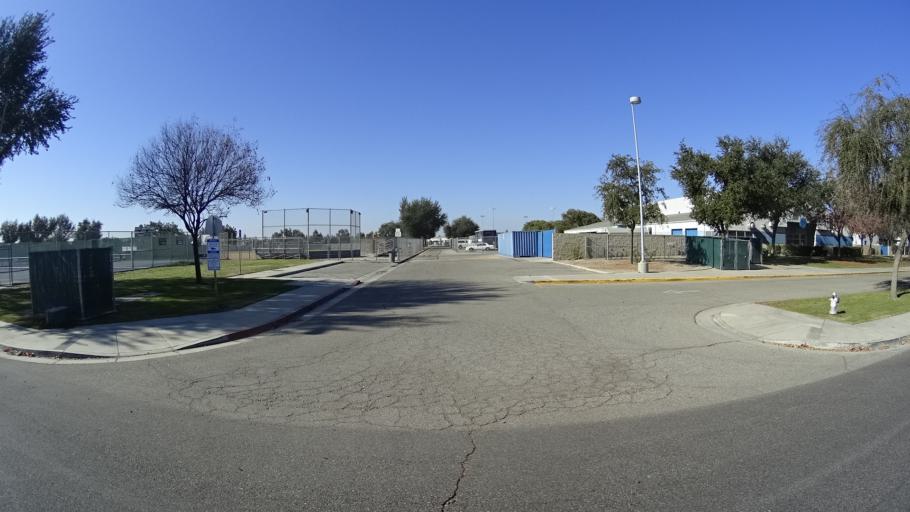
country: US
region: California
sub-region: Kern County
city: Rosedale
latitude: 35.3649
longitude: -119.1280
